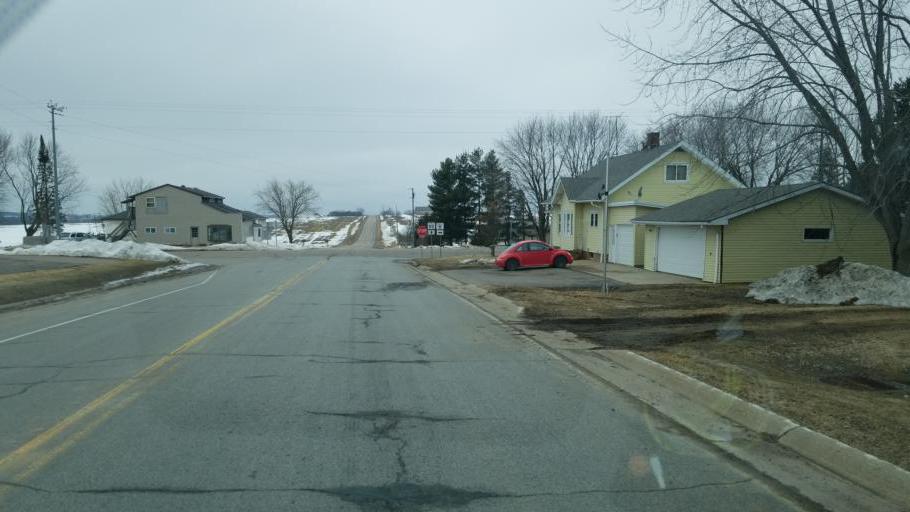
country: US
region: Wisconsin
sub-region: Wood County
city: Marshfield
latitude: 44.6271
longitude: -90.2175
